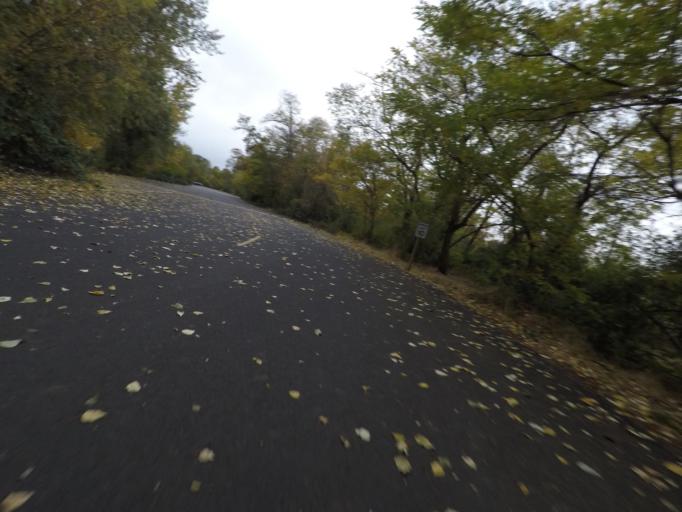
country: US
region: Washington
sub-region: Walla Walla County
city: Walla Walla East
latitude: 46.0822
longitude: -118.2540
